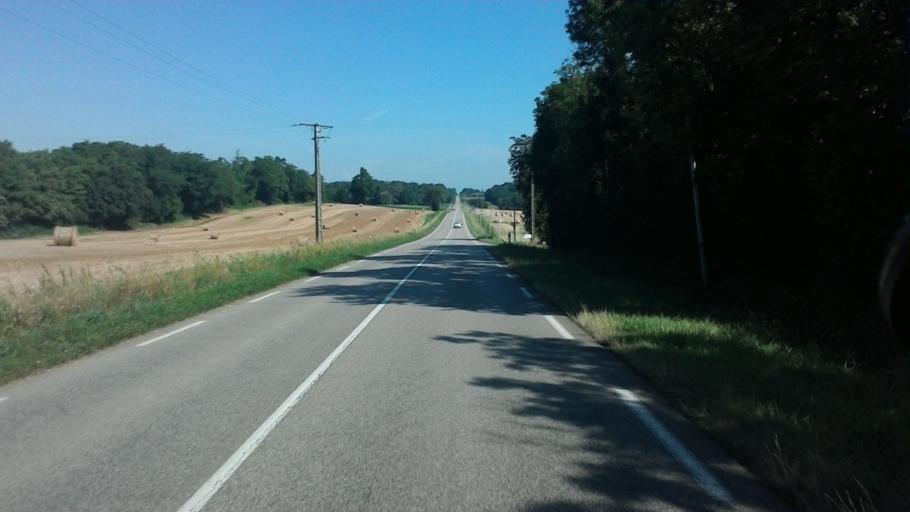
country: FR
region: Rhone-Alpes
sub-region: Departement de l'Ain
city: Saint-Trivier-de-Courtes
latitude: 46.4709
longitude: 5.0758
